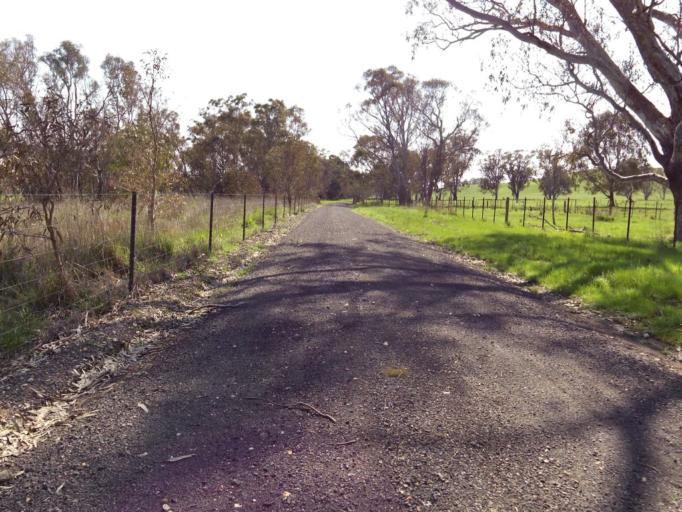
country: AU
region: Victoria
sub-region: Murrindindi
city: Alexandra
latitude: -37.1434
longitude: 145.5888
